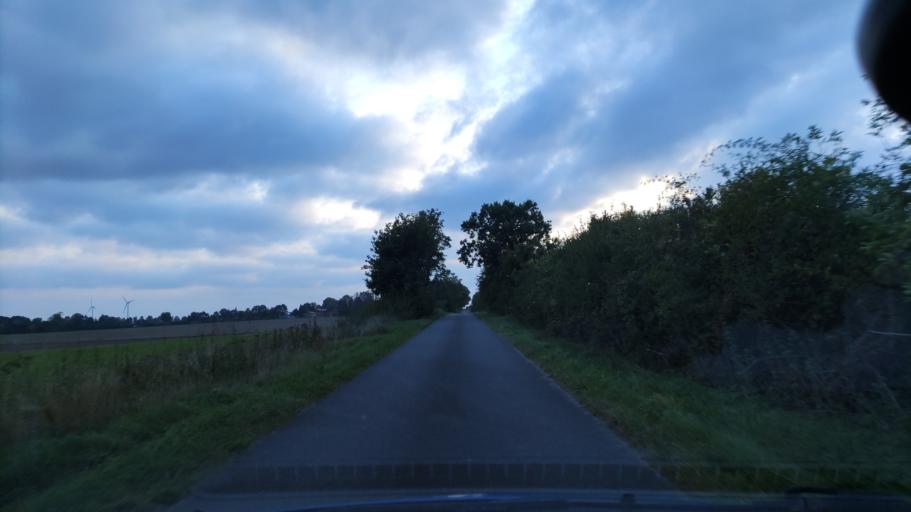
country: DE
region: Lower Saxony
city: Tosterglope
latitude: 53.2189
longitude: 10.8263
